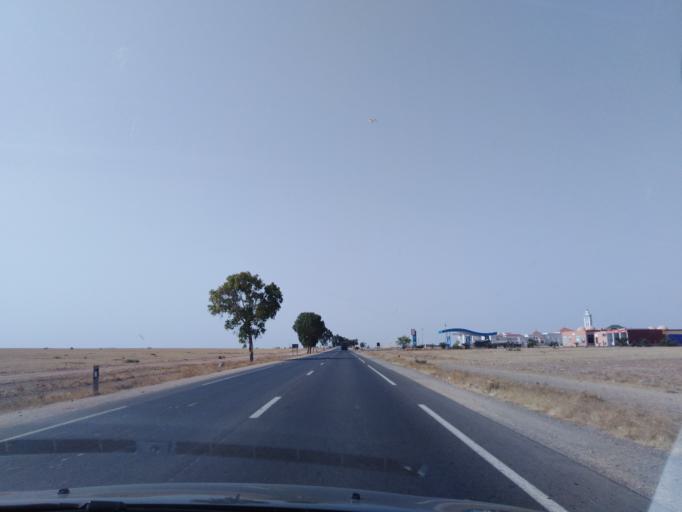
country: MA
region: Marrakech-Tensift-Al Haouz
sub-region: Kelaa-Des-Sraghna
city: Sidi Bou Othmane
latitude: 32.2159
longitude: -7.9569
